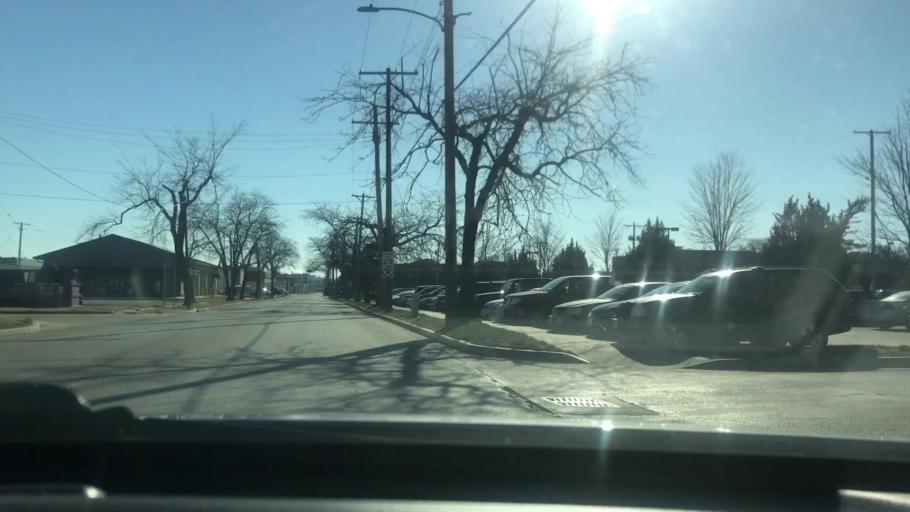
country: US
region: Missouri
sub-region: Clay County
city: North Kansas City
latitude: 39.1419
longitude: -94.5715
